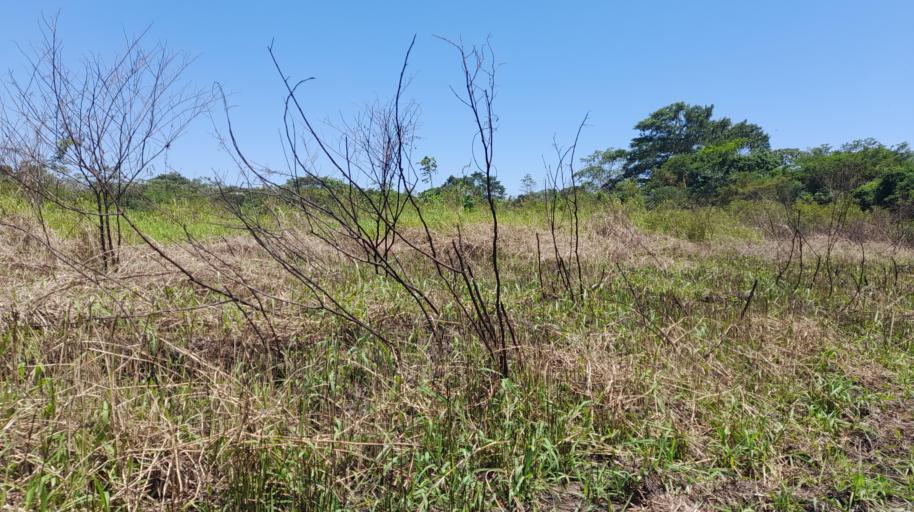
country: PE
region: Ucayali
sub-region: Provincia de Coronel Portillo
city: Puerto Callao
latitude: -8.2656
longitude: -74.6415
